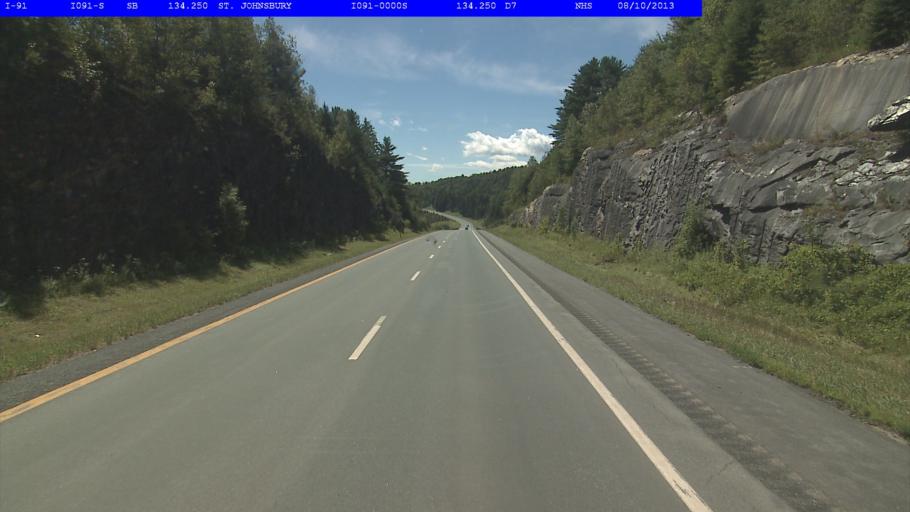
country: US
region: Vermont
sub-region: Caledonia County
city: Lyndon
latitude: 44.4785
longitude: -72.0238
